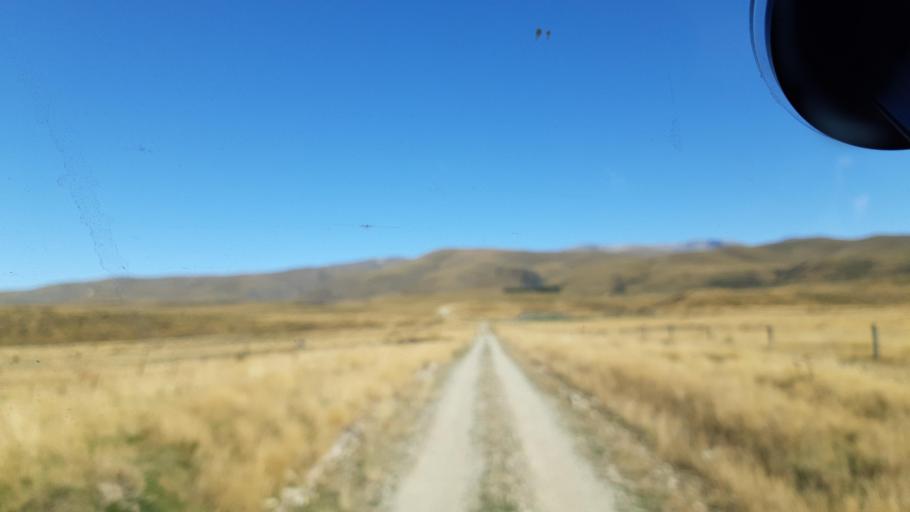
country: NZ
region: Otago
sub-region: Queenstown-Lakes District
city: Wanaka
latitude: -44.7791
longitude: 169.9113
